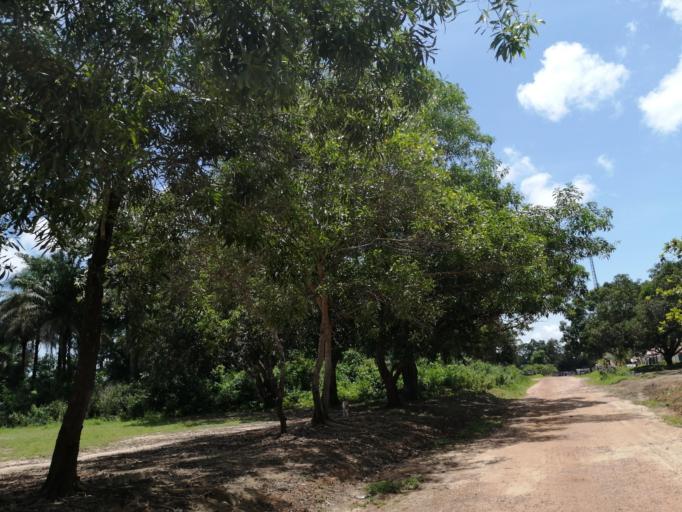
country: SL
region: Northern Province
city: Pepel
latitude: 8.6859
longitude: -12.9985
